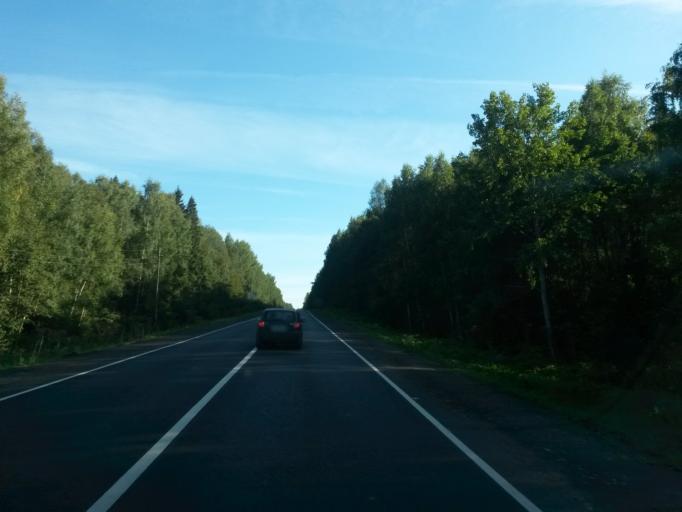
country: RU
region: Jaroslavl
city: Yaroslavl
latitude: 57.5049
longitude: 39.8985
